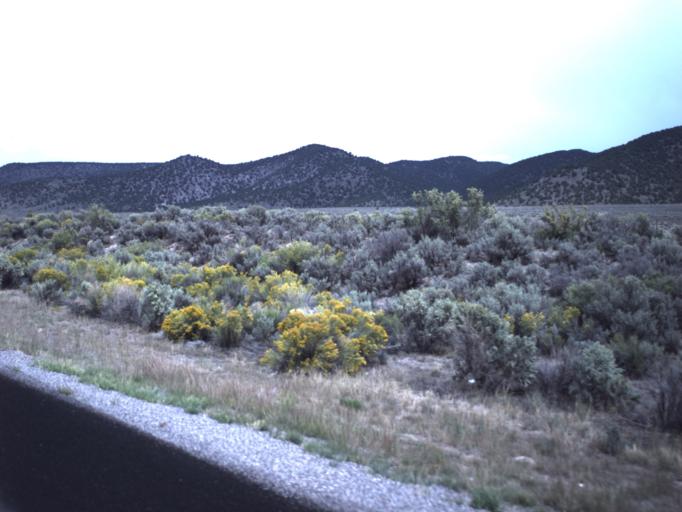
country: US
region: Utah
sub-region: Piute County
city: Junction
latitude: 38.0448
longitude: -112.3541
